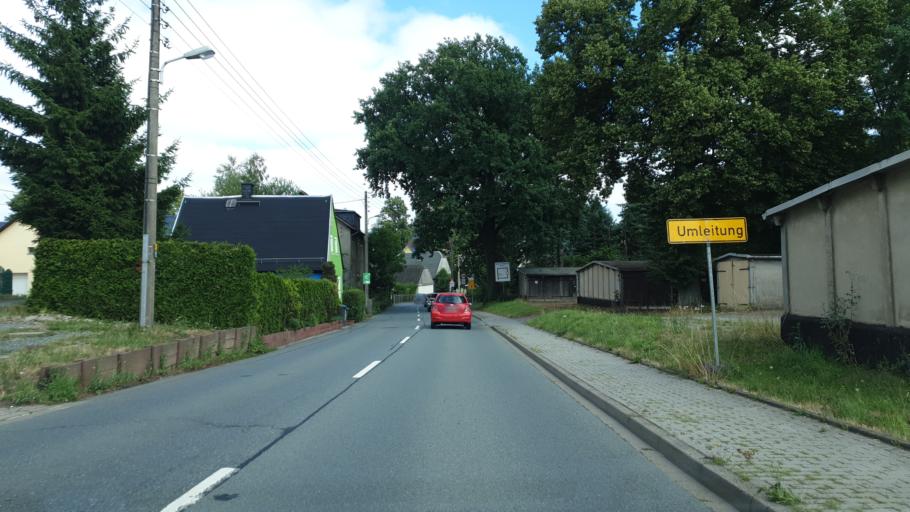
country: DE
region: Saxony
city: Neukirchen
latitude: 50.7978
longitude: 12.8582
